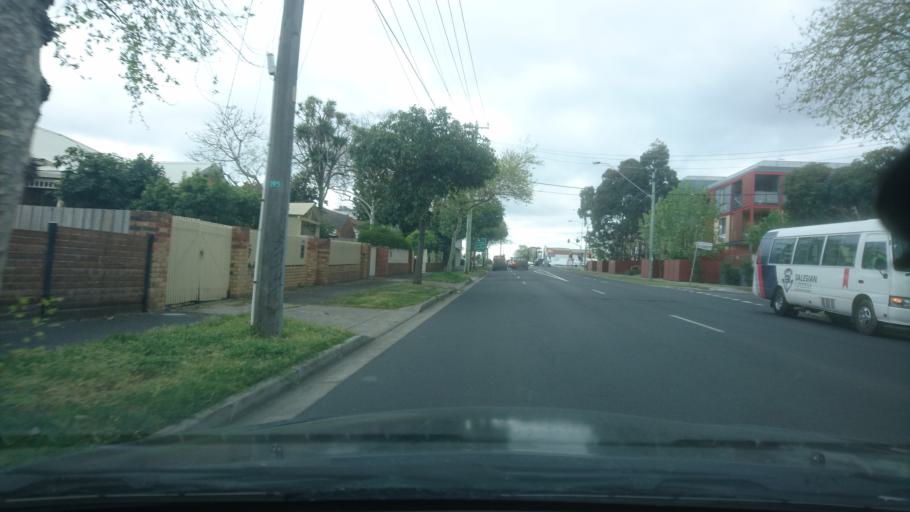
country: AU
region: Victoria
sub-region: Monash
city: Chadstone
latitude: -37.9022
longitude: 145.1052
